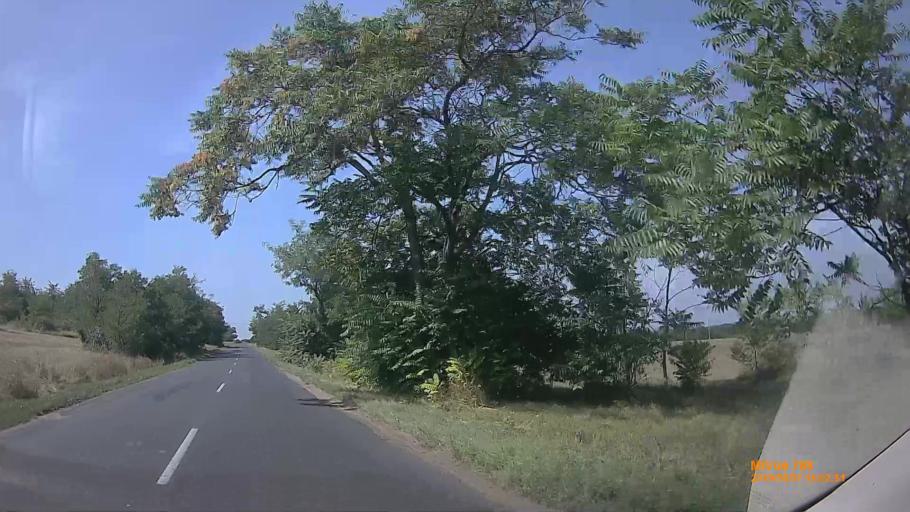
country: HU
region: Veszprem
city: Ajka
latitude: 47.0273
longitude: 17.5195
